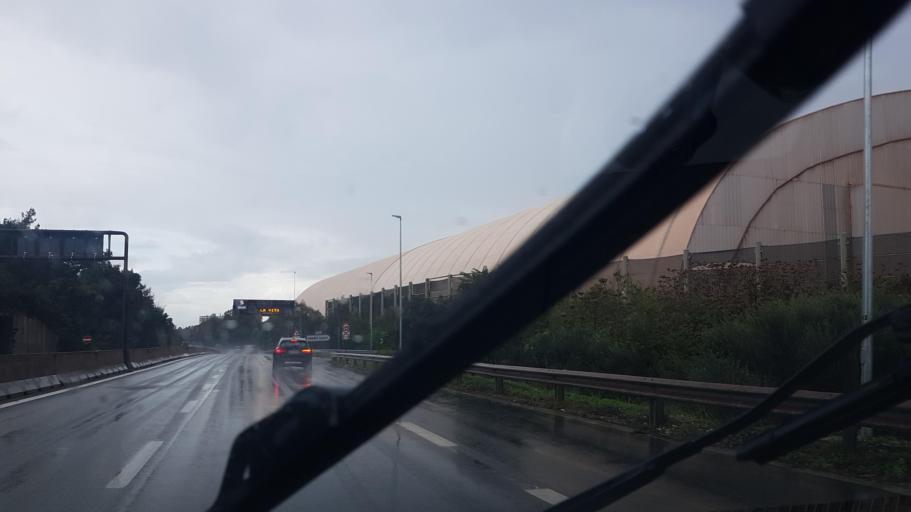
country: IT
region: Apulia
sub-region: Provincia di Taranto
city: Statte
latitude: 40.4975
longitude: 17.2253
